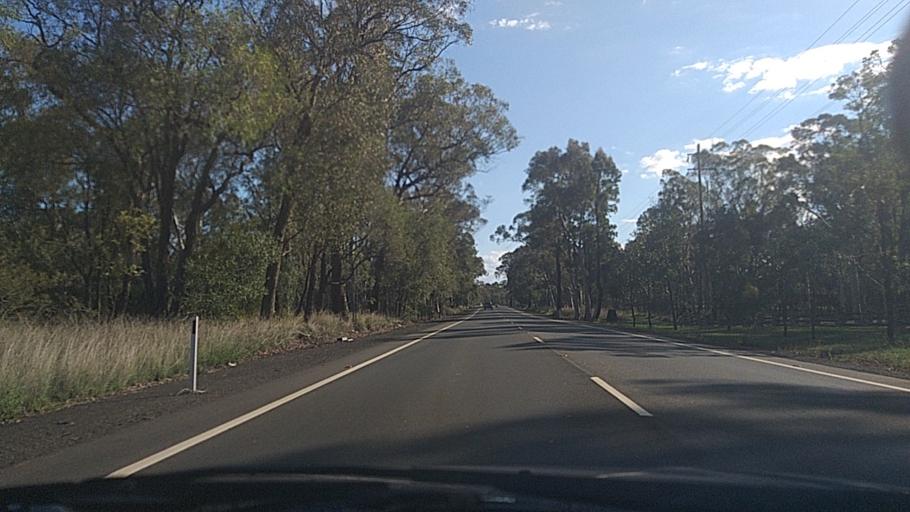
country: AU
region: New South Wales
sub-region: Hawkesbury
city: South Windsor
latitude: -33.6537
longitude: 150.7727
